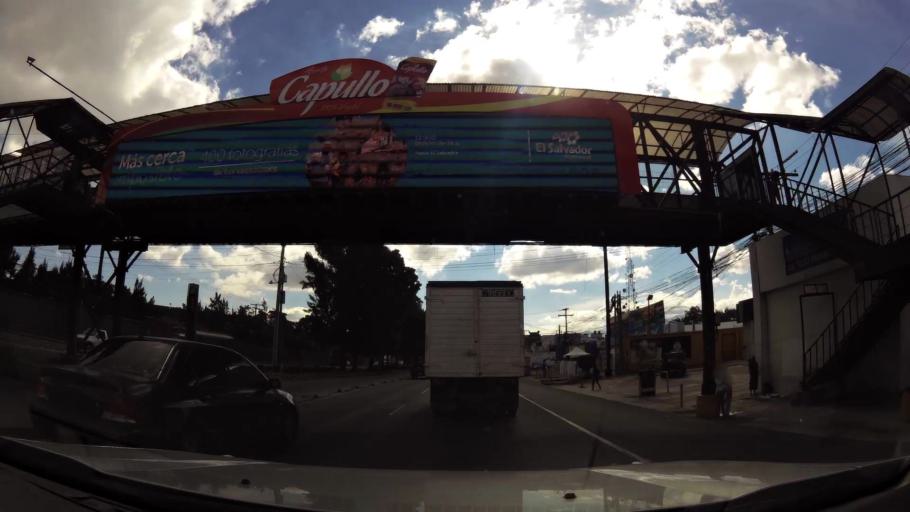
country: GT
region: Guatemala
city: Mixco
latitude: 14.5870
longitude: -90.5629
